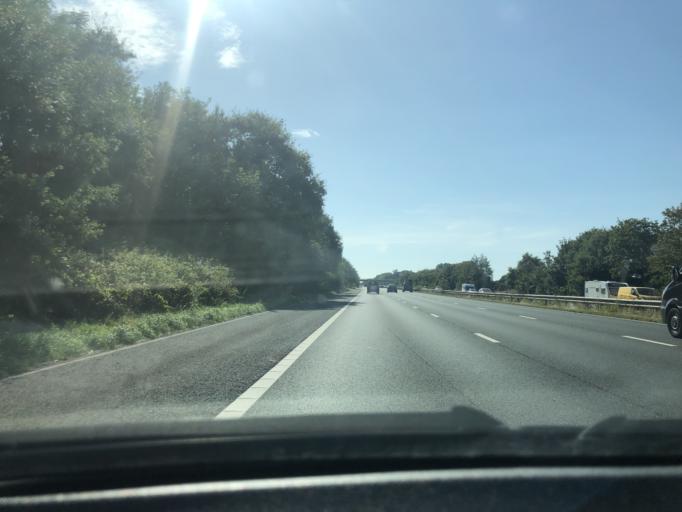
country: GB
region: England
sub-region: Devon
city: Uffculme
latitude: 50.9573
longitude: -3.2415
